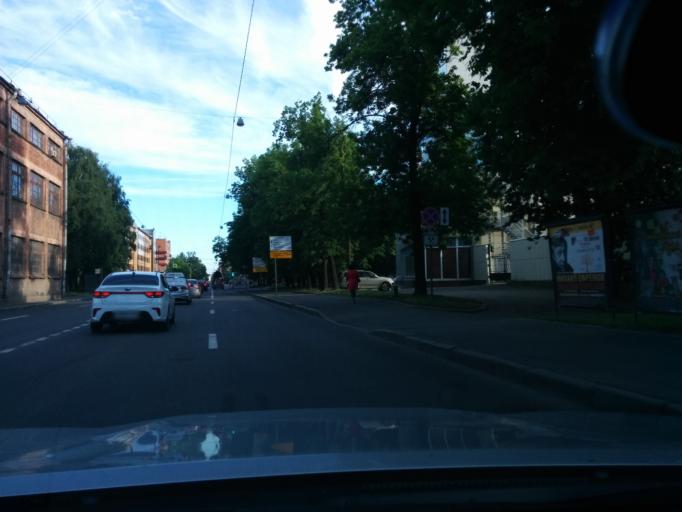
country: RU
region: Leningrad
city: Sampsonievskiy
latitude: 59.9808
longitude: 30.3367
